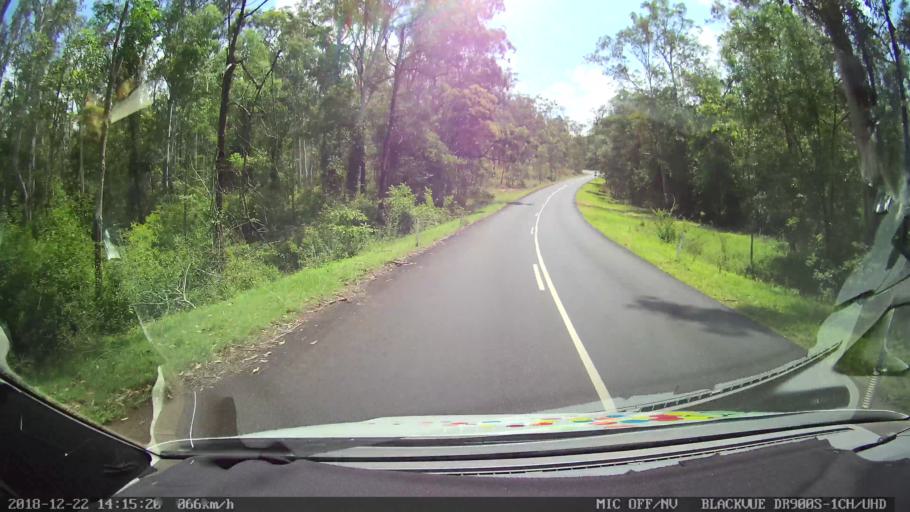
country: AU
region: New South Wales
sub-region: Clarence Valley
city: Coutts Crossing
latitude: -30.0018
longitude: 152.6794
